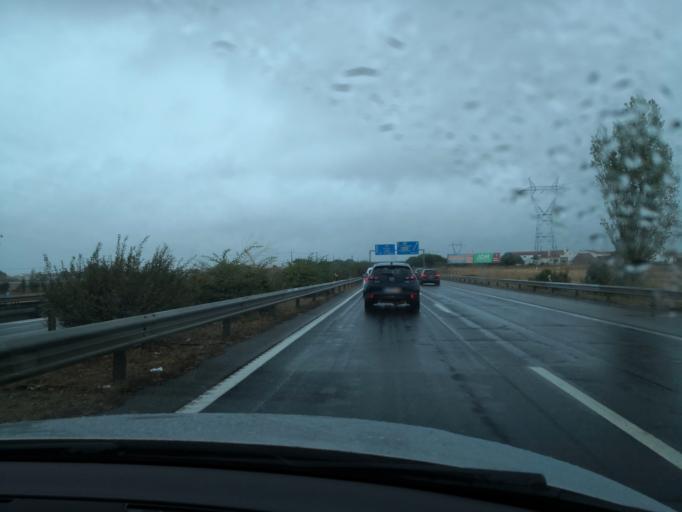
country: PT
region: Setubal
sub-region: Montijo
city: Montijo
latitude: 38.6704
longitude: -8.9516
